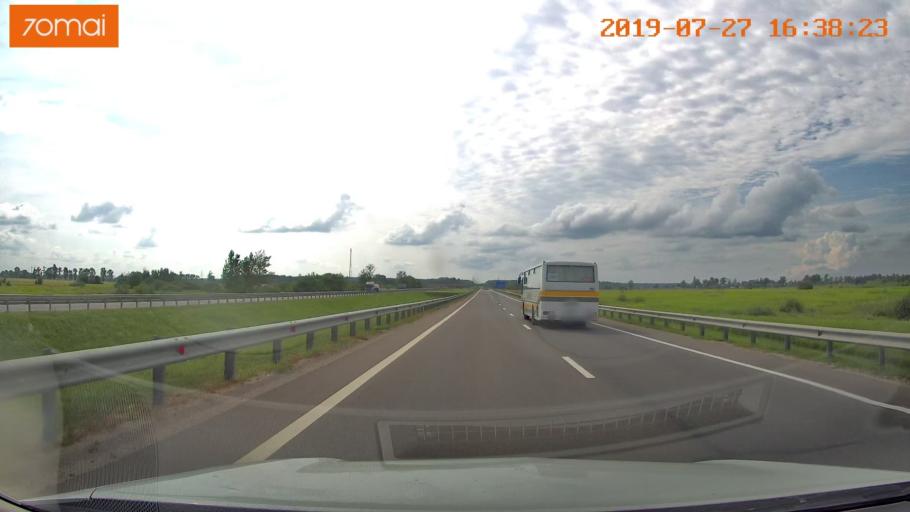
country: RU
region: Kaliningrad
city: Gvardeysk
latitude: 54.6488
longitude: 21.2297
